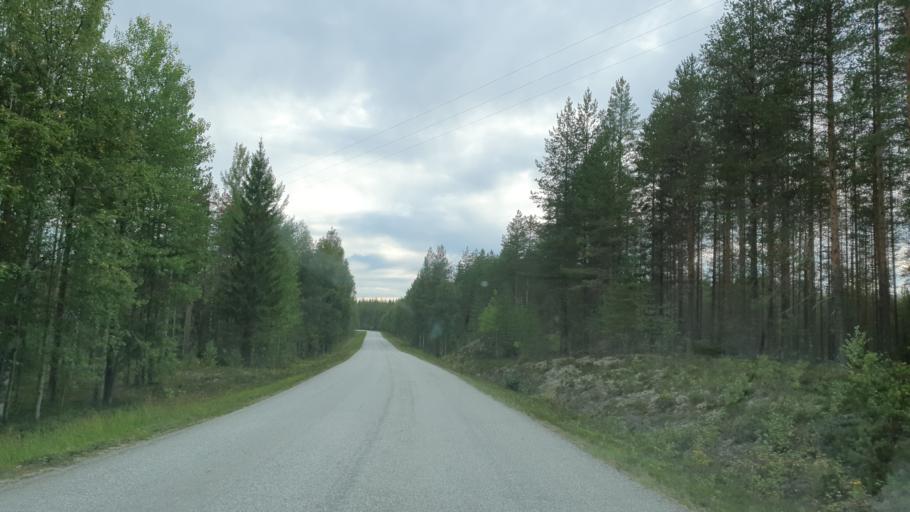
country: FI
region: Kainuu
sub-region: Kehys-Kainuu
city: Kuhmo
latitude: 64.1880
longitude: 29.3587
